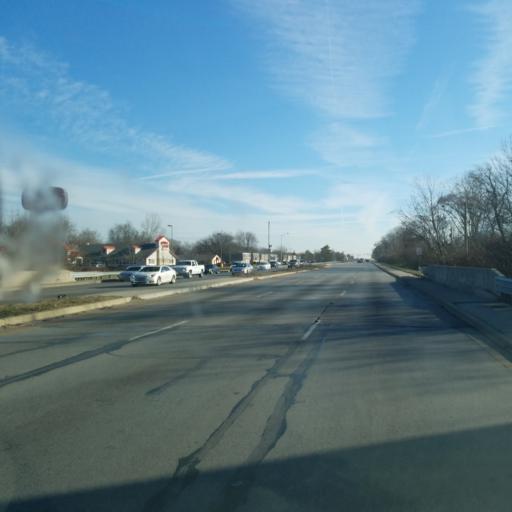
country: US
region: Indiana
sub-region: Marion County
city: Speedway
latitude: 39.8234
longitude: -86.2682
